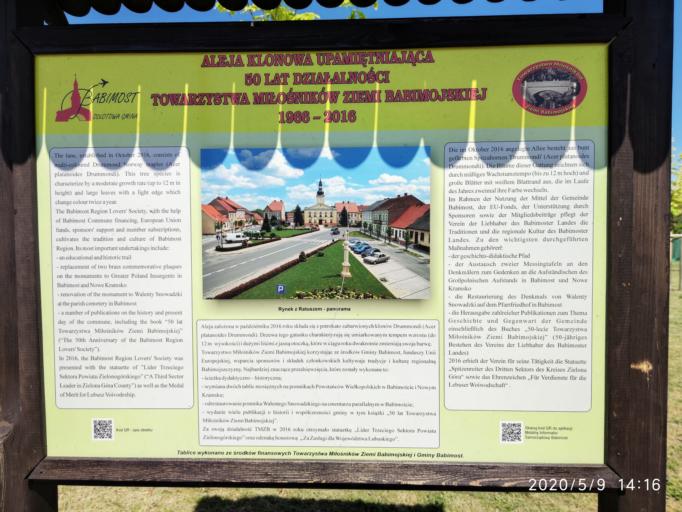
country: PL
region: Lubusz
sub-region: Powiat zielonogorski
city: Babimost
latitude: 52.1654
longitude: 15.8365
